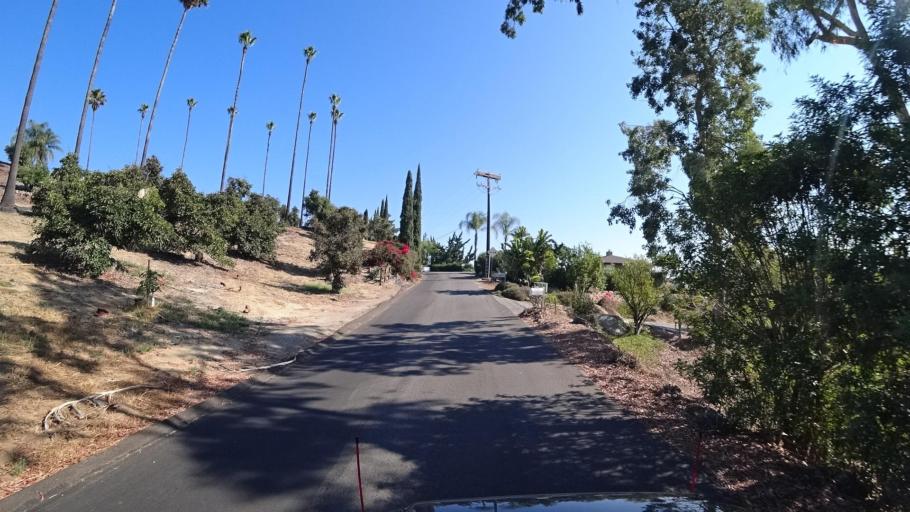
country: US
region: California
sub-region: San Diego County
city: Fallbrook
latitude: 33.3997
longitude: -117.2332
